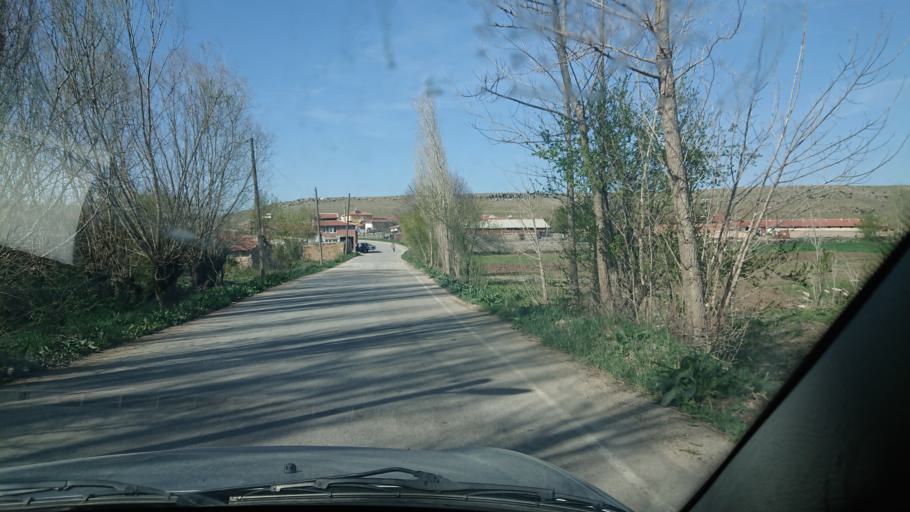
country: TR
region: Eskisehir
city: Eskisehir
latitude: 39.6785
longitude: 30.4857
